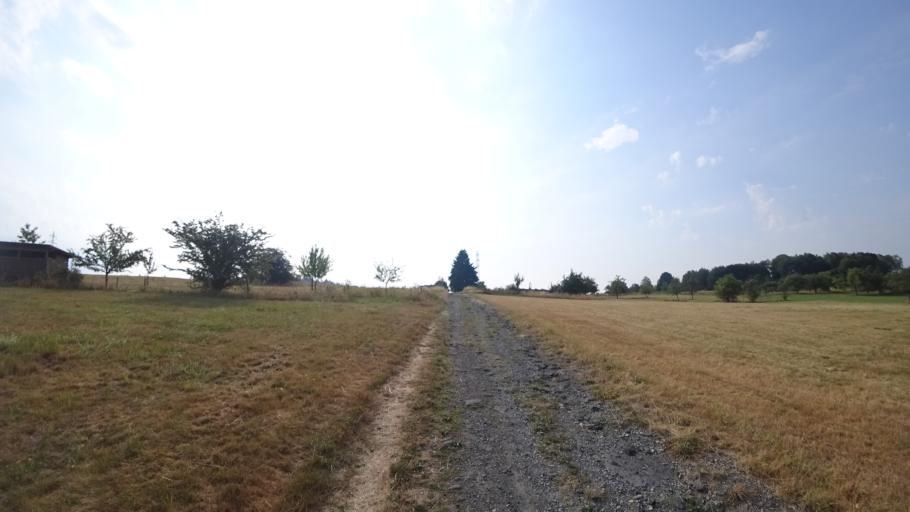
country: DE
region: Rheinland-Pfalz
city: Hilgert
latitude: 50.4610
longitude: 7.6841
